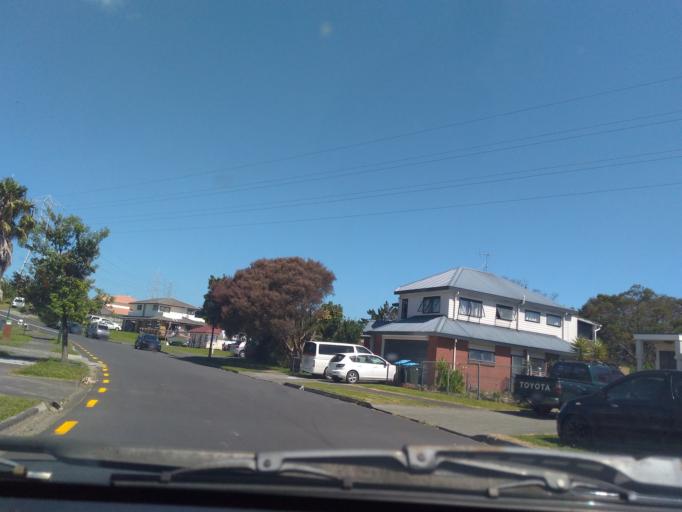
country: NZ
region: Auckland
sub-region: Auckland
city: Rosebank
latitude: -36.9006
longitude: 174.6862
